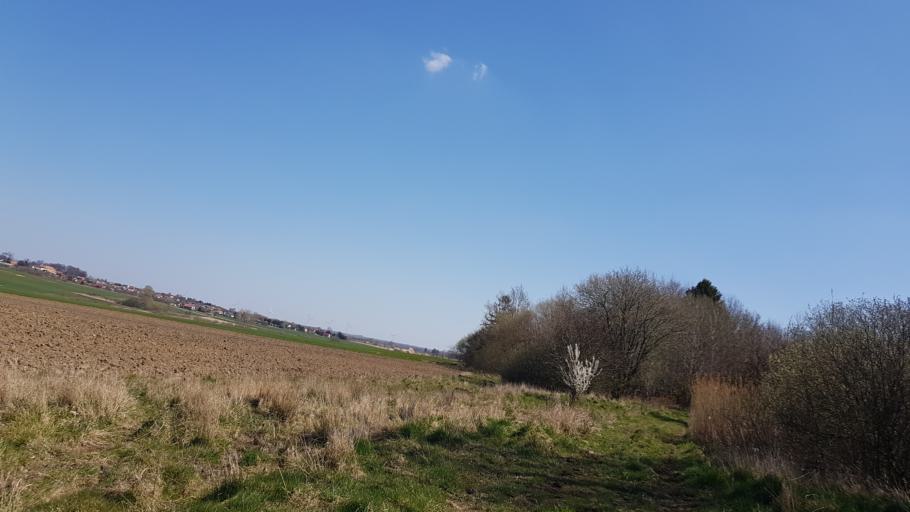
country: PL
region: Pomeranian Voivodeship
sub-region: Powiat slupski
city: Ustka
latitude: 54.5145
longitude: 16.7407
